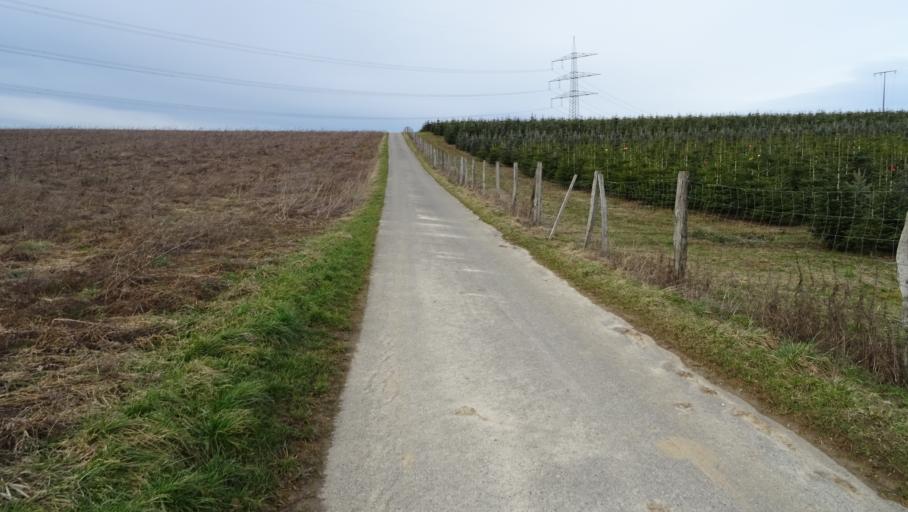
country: DE
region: Baden-Wuerttemberg
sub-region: Karlsruhe Region
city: Billigheim
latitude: 49.3650
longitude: 9.2204
